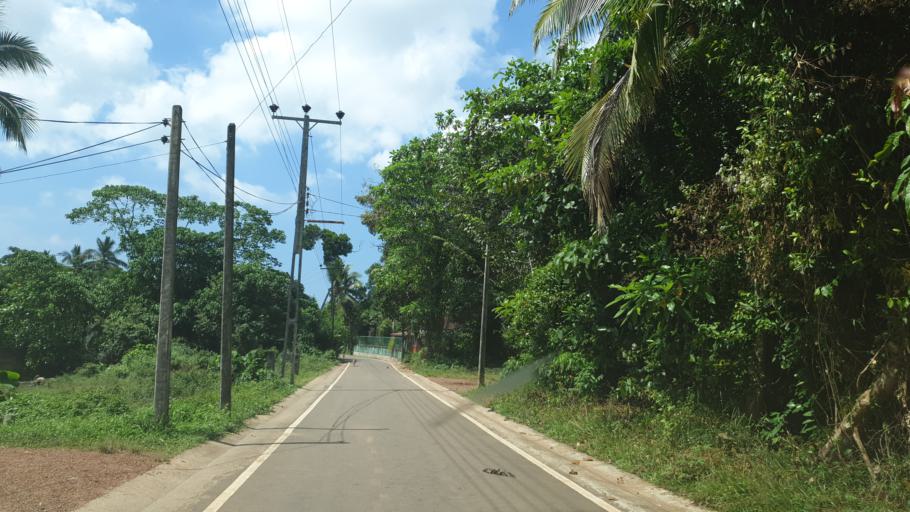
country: LK
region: Western
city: Panadura
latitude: 6.6757
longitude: 79.9675
